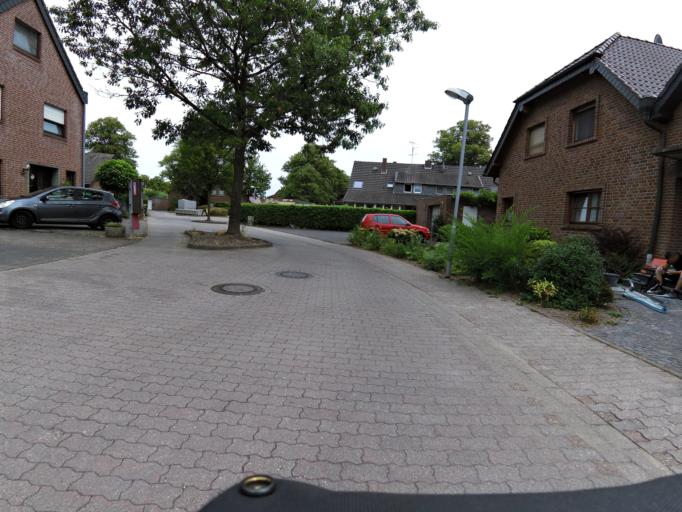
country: DE
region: North Rhine-Westphalia
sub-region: Regierungsbezirk Dusseldorf
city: Kevelaer
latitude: 51.5843
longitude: 6.2316
